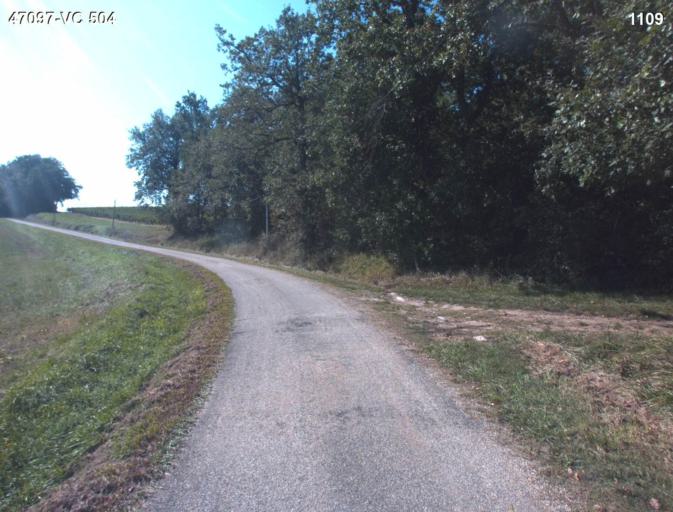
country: FR
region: Aquitaine
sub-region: Departement du Lot-et-Garonne
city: Vianne
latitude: 44.1855
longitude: 0.3468
